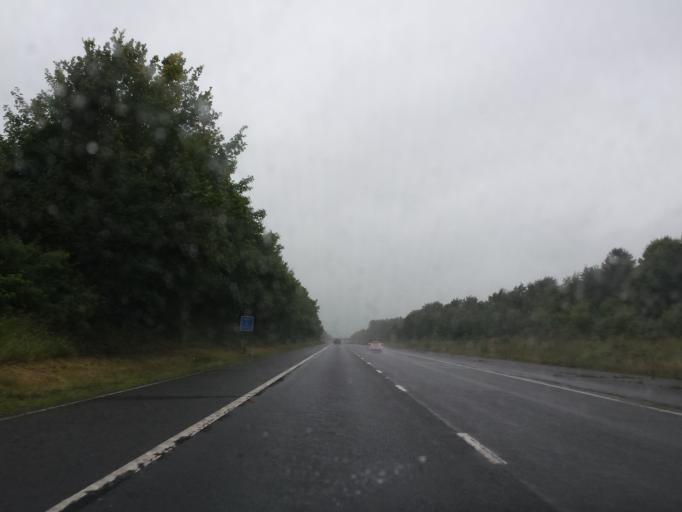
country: GB
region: England
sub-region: Leicestershire
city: Enderby
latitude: 52.5994
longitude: -1.2080
